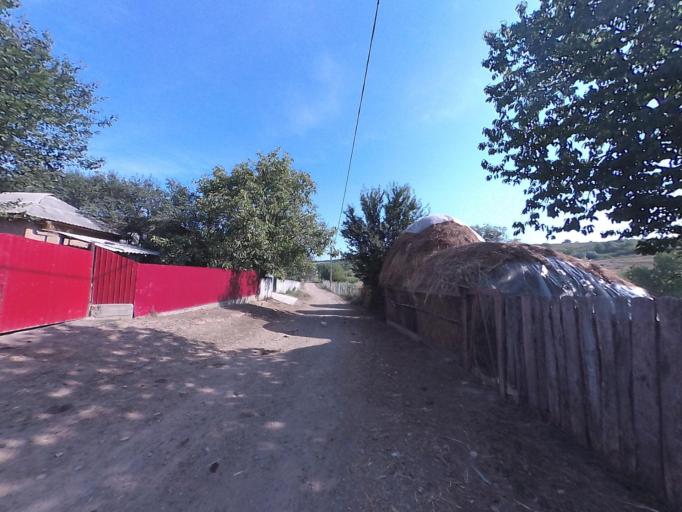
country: RO
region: Vaslui
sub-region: Comuna Osesti
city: Buda
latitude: 46.7650
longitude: 27.4299
